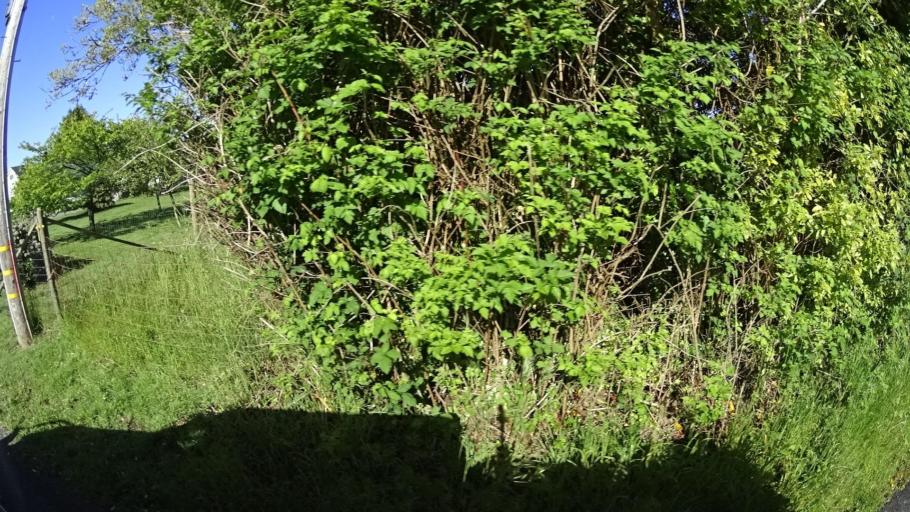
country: US
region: California
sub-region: Humboldt County
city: McKinleyville
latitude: 40.9890
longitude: -124.1005
